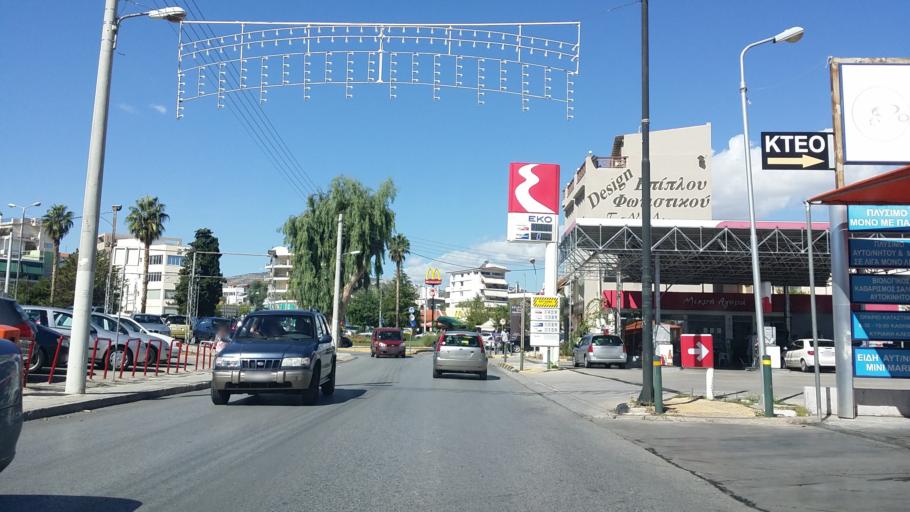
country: GR
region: Attica
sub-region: Nomarchia Athinas
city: Agioi Anargyroi
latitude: 38.0303
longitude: 23.7138
